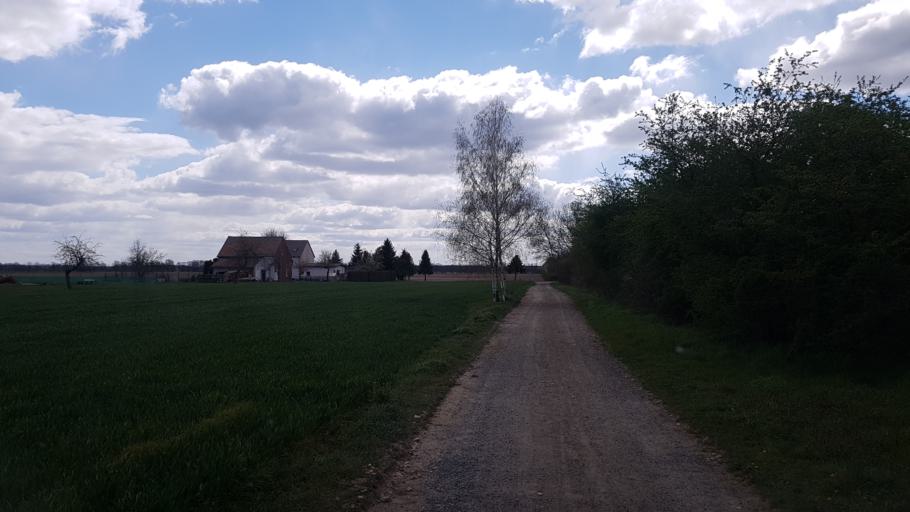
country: DE
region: Brandenburg
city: Sonnewalde
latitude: 51.6822
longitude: 13.6492
